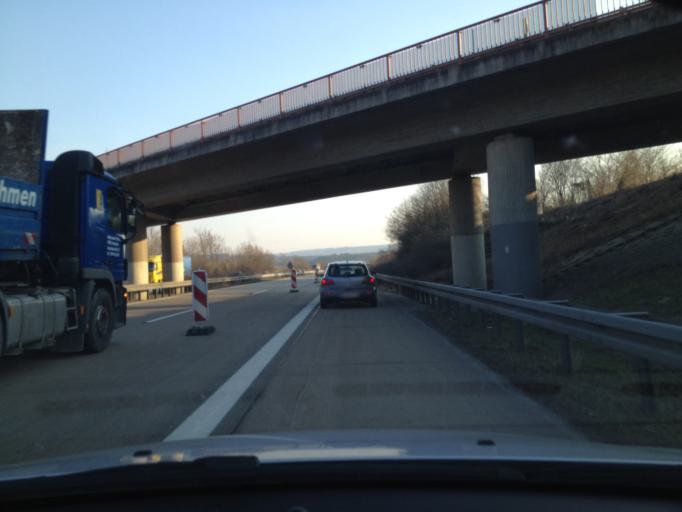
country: DE
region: Baden-Wuerttemberg
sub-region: Regierungsbezirk Stuttgart
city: Westhausen
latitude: 48.9334
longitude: 10.1942
